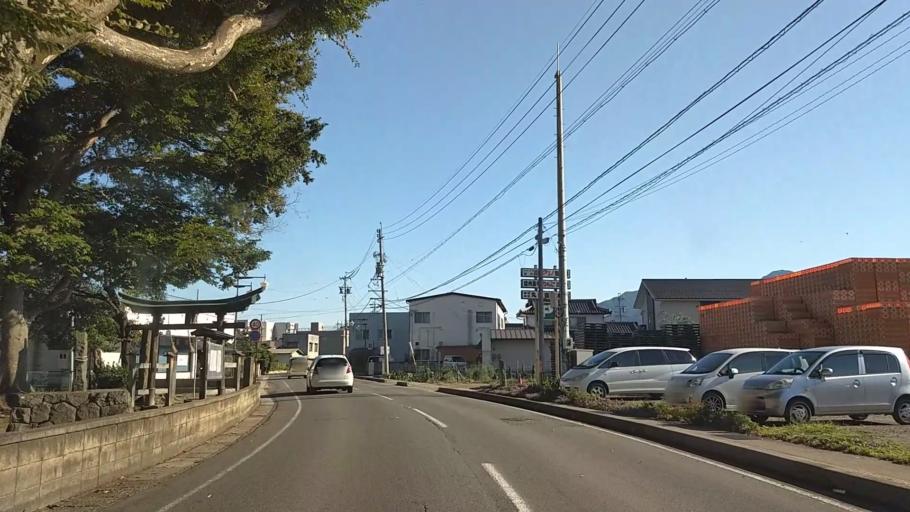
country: JP
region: Nagano
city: Nagano-shi
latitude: 36.5331
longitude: 138.1206
